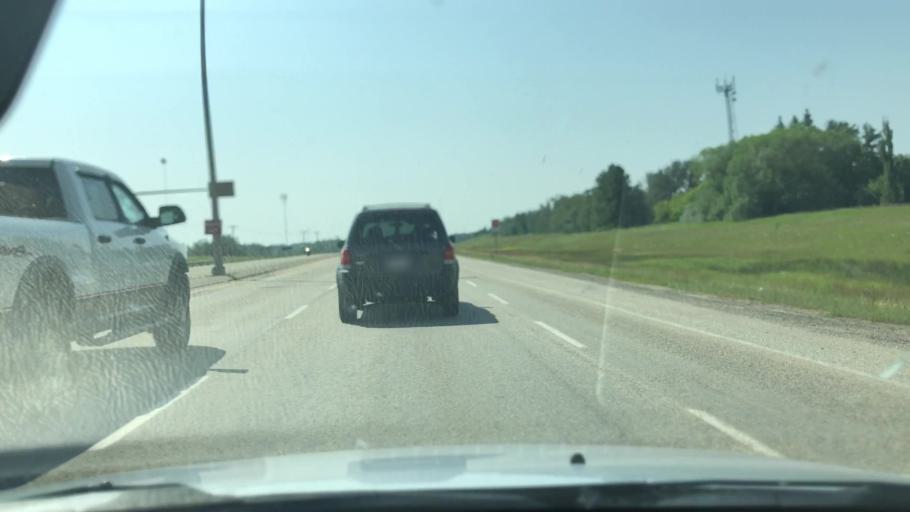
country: CA
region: Alberta
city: Devon
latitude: 53.4538
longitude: -113.7623
